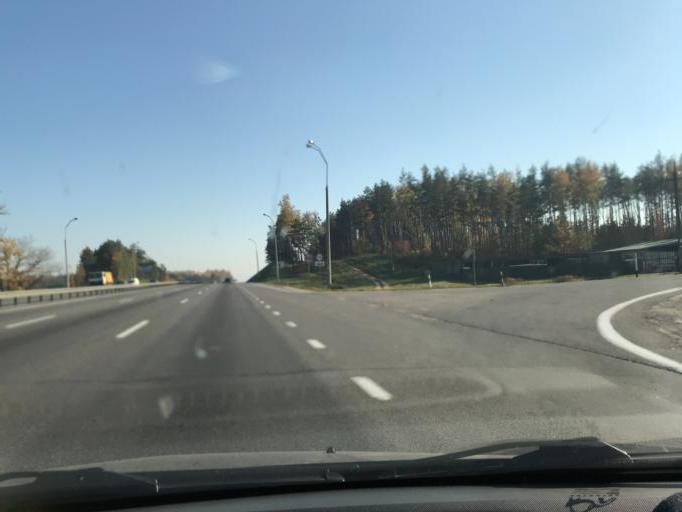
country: BY
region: Minsk
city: Pryvol'ny
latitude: 53.8200
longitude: 27.7632
